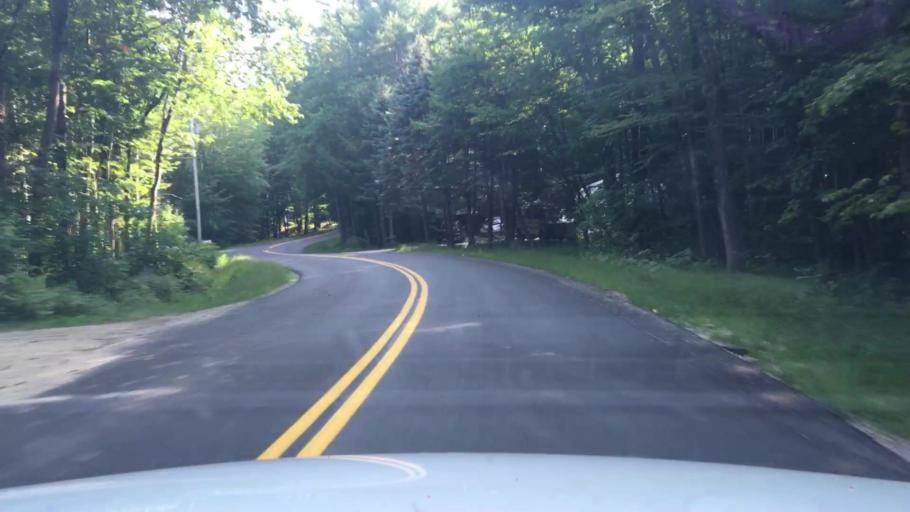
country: US
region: Maine
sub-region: Cumberland County
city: New Gloucester
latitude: 43.9417
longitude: -70.2880
